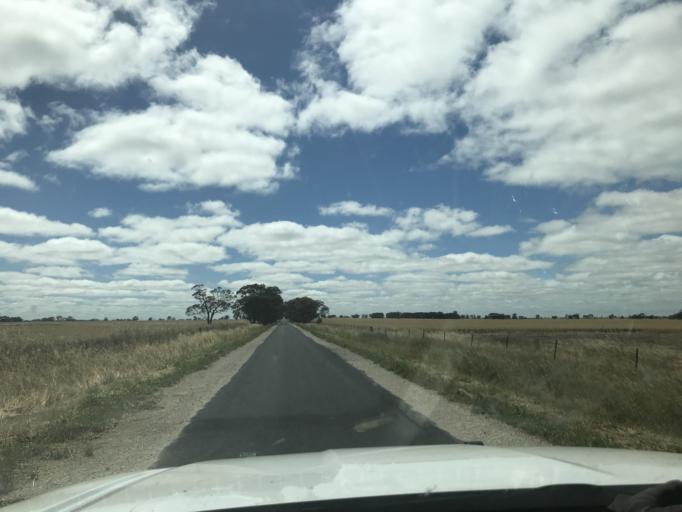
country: AU
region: South Australia
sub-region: Tatiara
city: Bordertown
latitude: -36.2779
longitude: 141.1092
